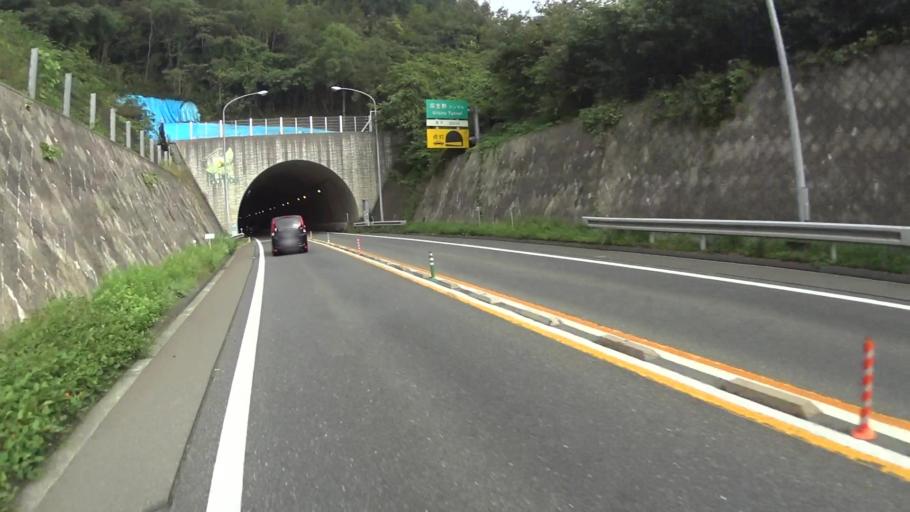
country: JP
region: Kyoto
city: Kameoka
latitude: 35.1246
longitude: 135.4783
